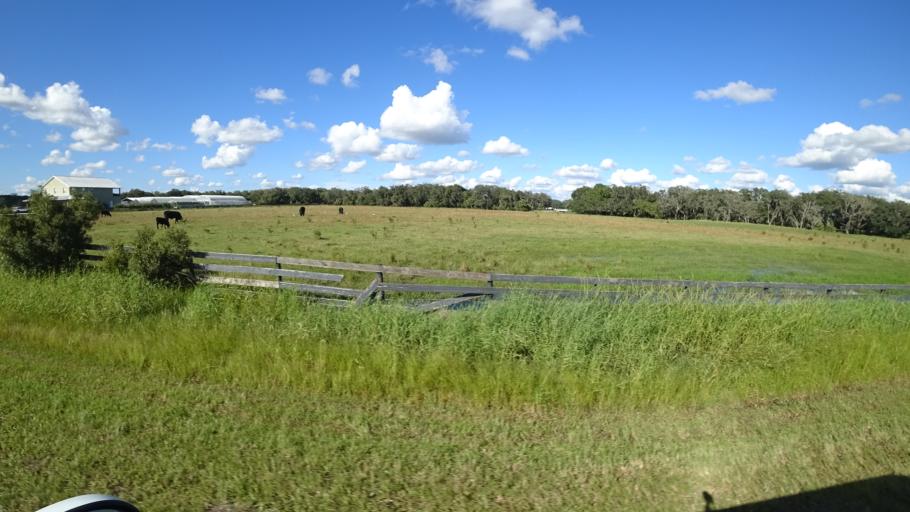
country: US
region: Florida
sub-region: Sarasota County
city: Lake Sarasota
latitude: 27.2889
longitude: -82.2198
